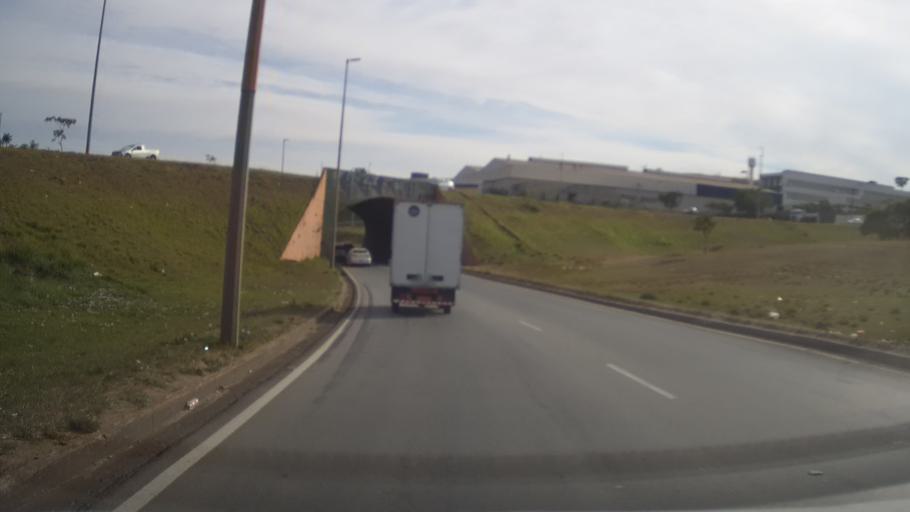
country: BR
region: Minas Gerais
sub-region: Contagem
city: Contagem
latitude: -19.9179
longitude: -44.0558
